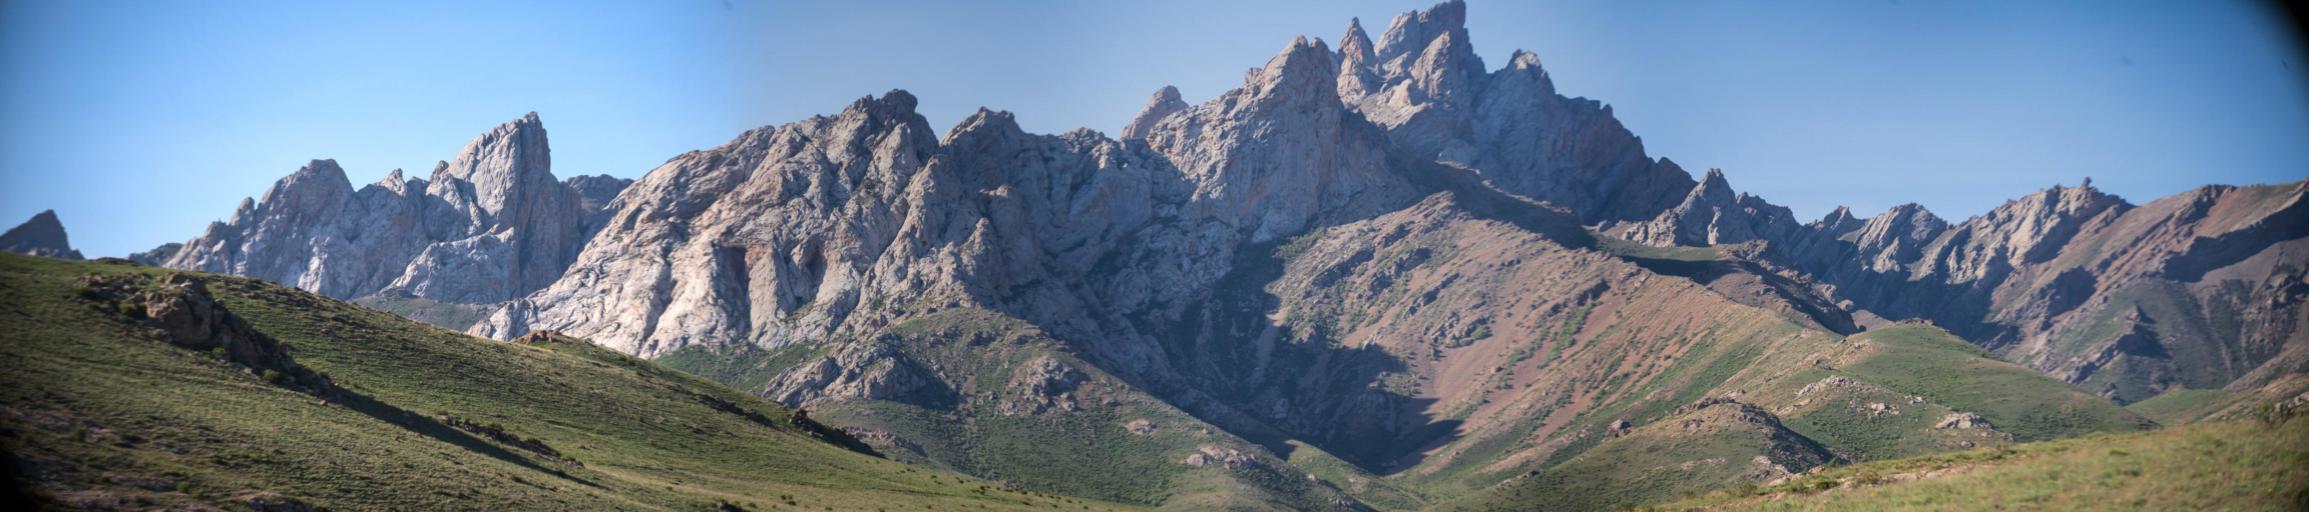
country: KZ
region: Ongtustik Qazaqstan
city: Ashchysay
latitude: 43.8033
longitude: 68.7941
